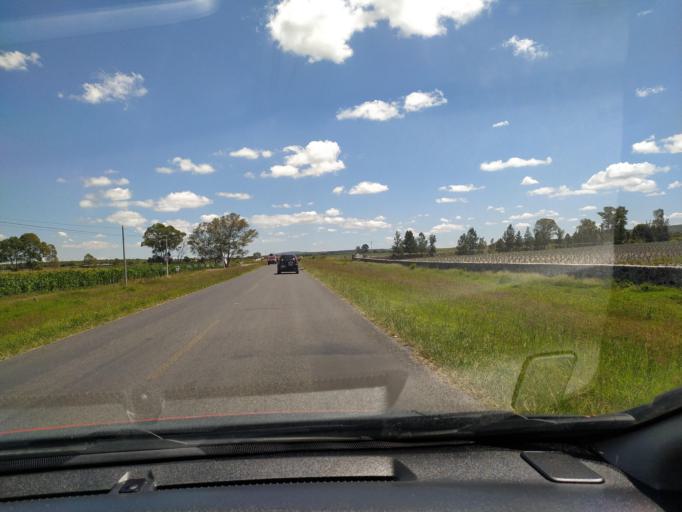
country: MX
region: Jalisco
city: San Diego de Alejandria
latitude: 21.0053
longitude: -102.0667
